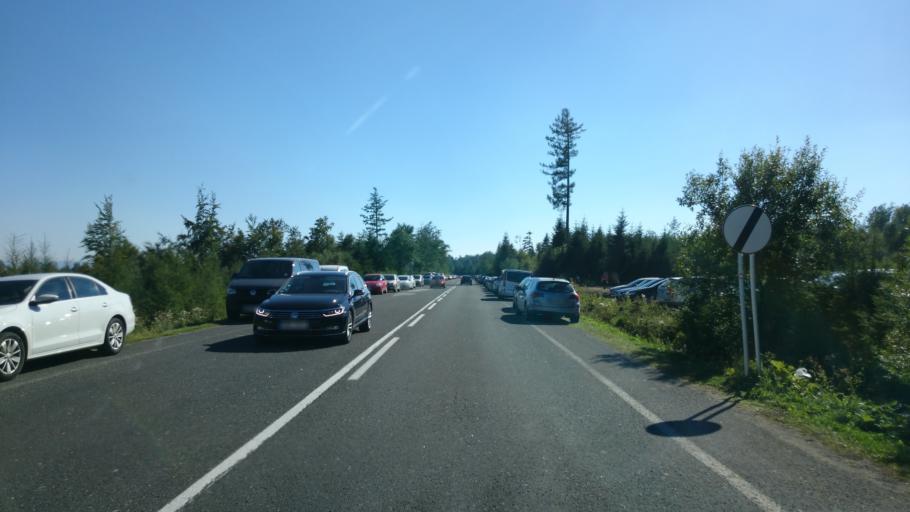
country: SK
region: Presovsky
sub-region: Okres Poprad
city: Nova Lesna
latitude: 49.1873
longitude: 20.2923
